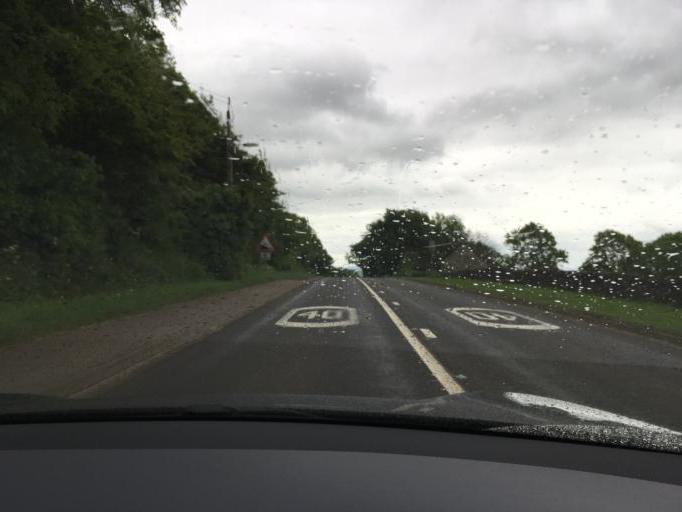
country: GB
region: England
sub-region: Staffordshire
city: Mayfield
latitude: 53.0291
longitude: -1.7988
